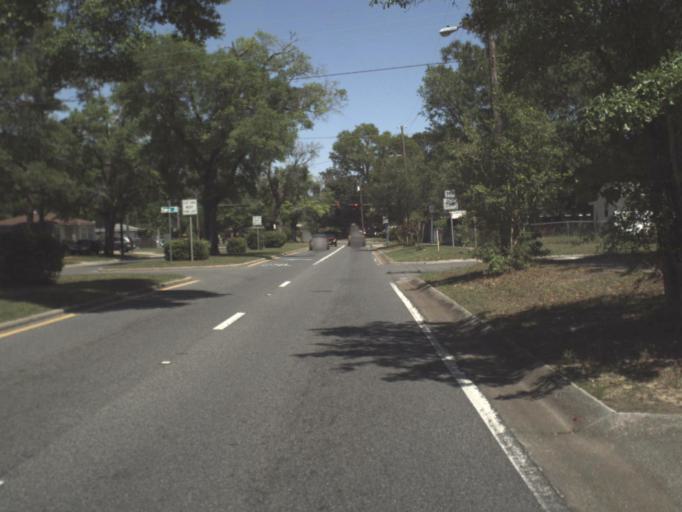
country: US
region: Florida
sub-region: Escambia County
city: Goulding
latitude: 30.4472
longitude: -87.2140
